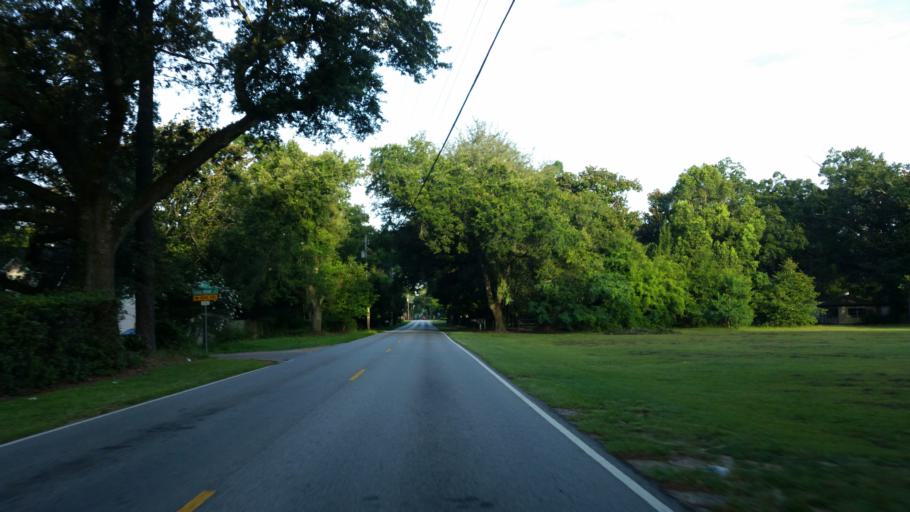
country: US
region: Florida
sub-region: Escambia County
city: Ensley
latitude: 30.5198
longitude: -87.3169
